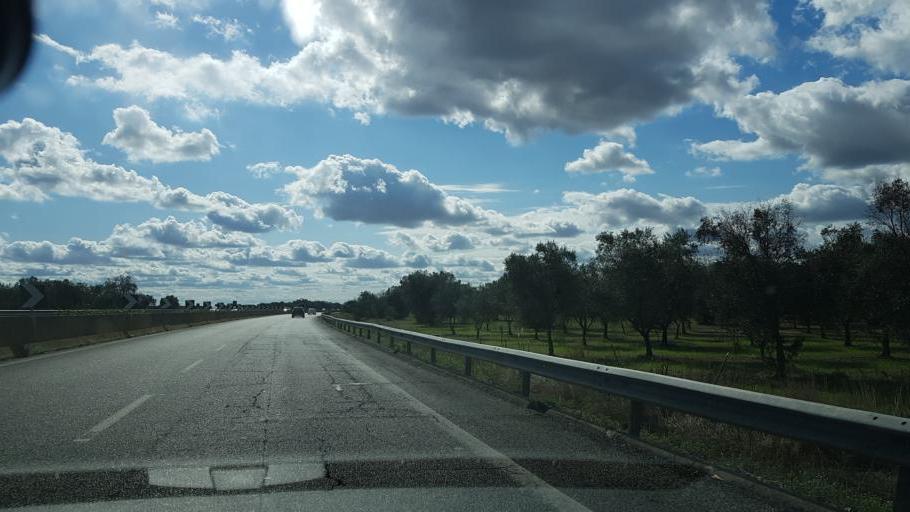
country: IT
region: Apulia
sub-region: Provincia di Brindisi
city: San Pietro Vernotico
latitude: 40.5339
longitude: 18.0083
